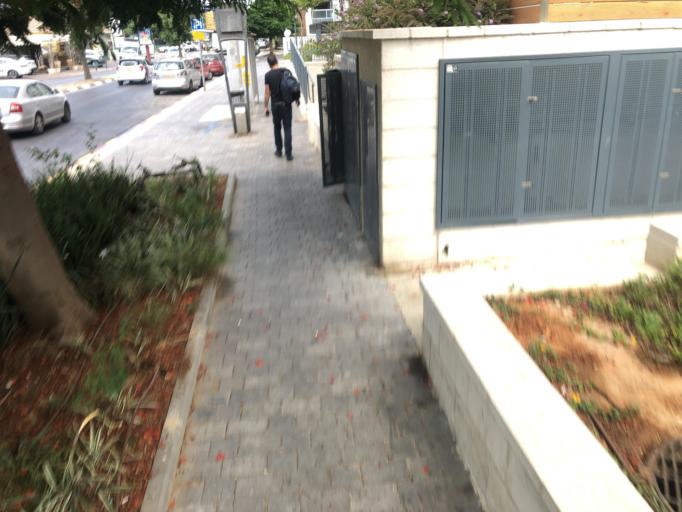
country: IL
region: Central District
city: Yehud
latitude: 32.0283
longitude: 34.8891
